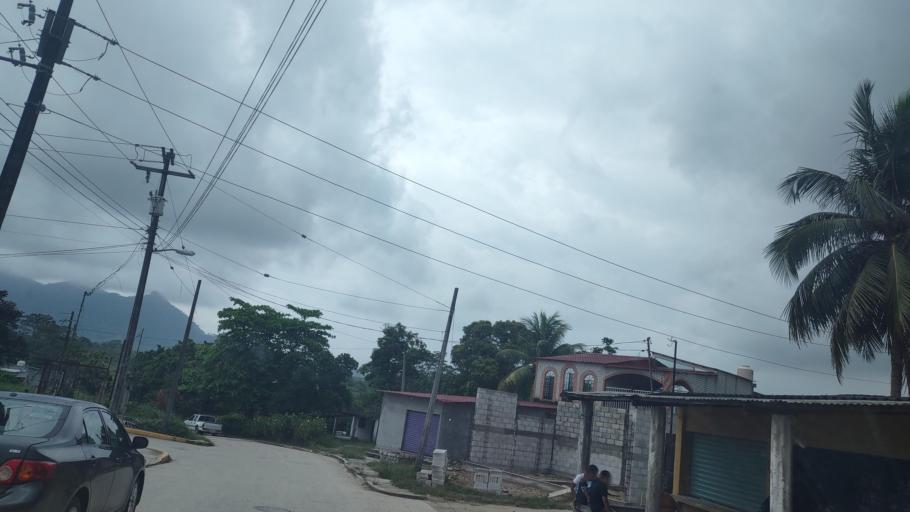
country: MX
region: Veracruz
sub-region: Uxpanapa
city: Poblado 10
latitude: 17.4973
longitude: -94.1626
